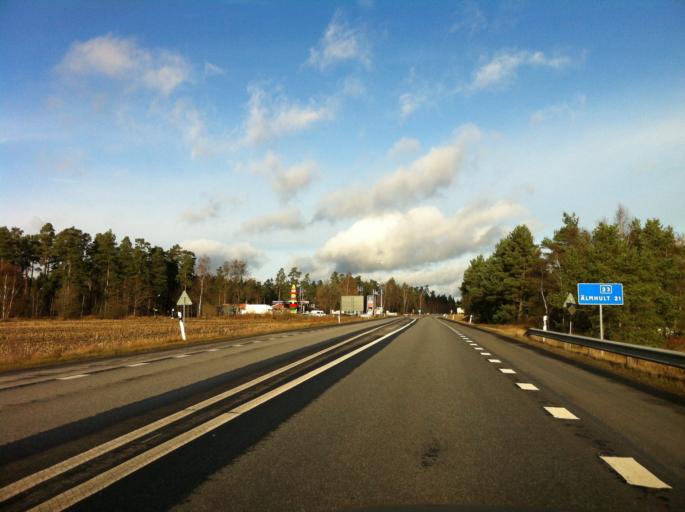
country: SE
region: Skane
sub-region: Osby Kommun
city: Osby
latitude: 56.3912
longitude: 14.0371
